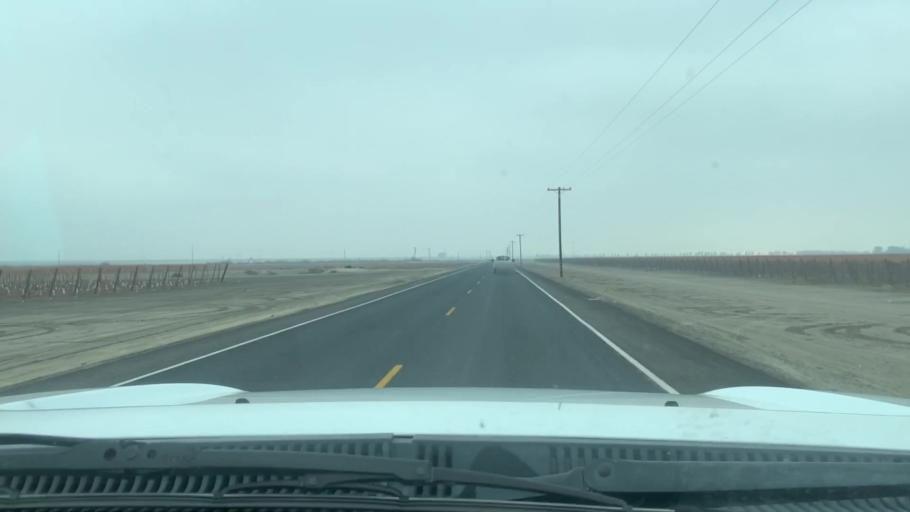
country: US
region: California
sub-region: Kern County
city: Buttonwillow
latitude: 35.4995
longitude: -119.5742
